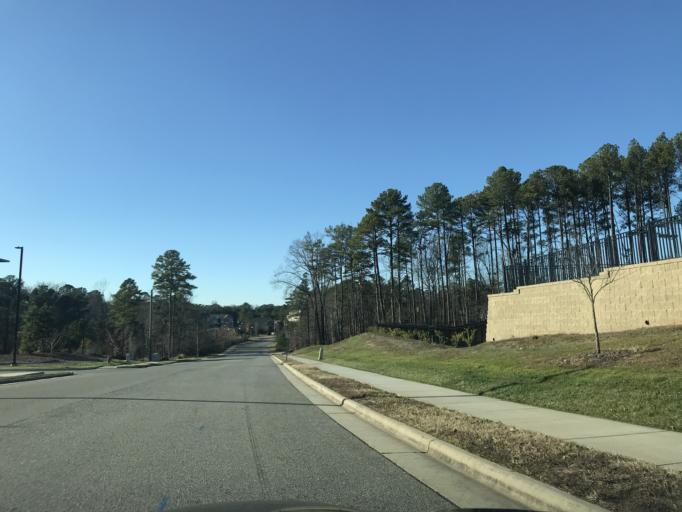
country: US
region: North Carolina
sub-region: Wake County
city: Morrisville
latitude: 35.8960
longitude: -78.8064
